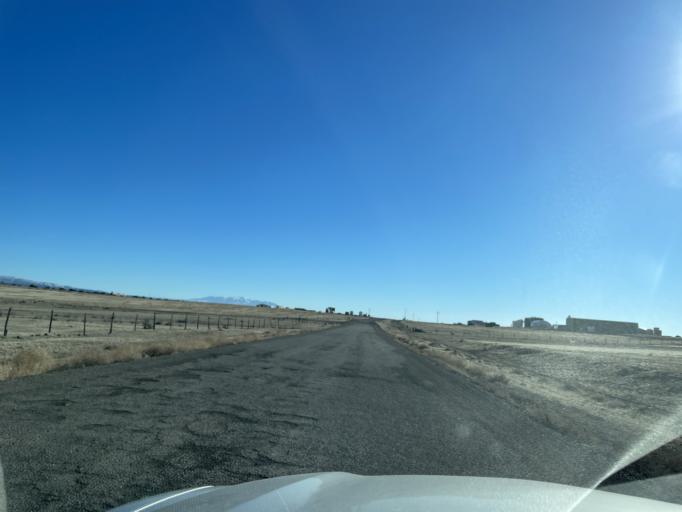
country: US
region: Colorado
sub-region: Mesa County
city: Loma
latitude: 39.1775
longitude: -109.1317
